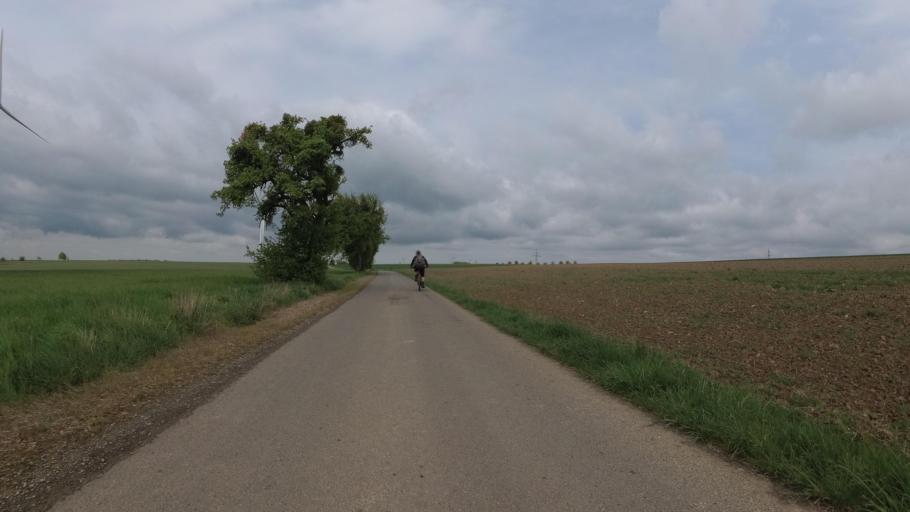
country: DE
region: Saarland
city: Orscholz
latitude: 49.4372
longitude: 6.5217
